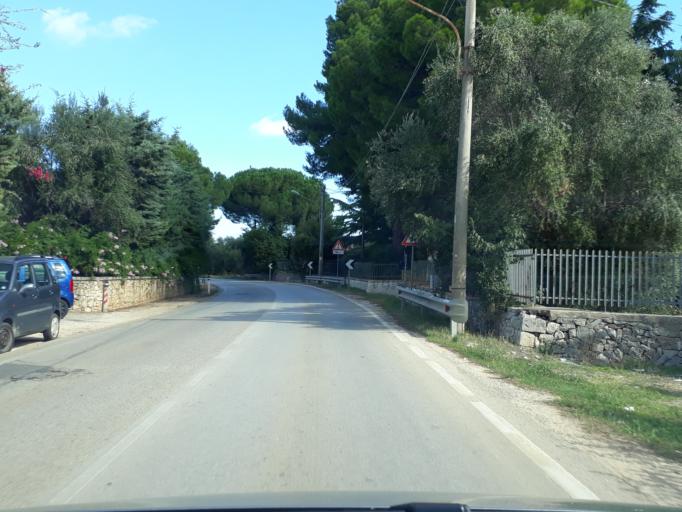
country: IT
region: Apulia
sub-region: Provincia di Bari
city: Mola di Bari
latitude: 41.0354
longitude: 17.0478
